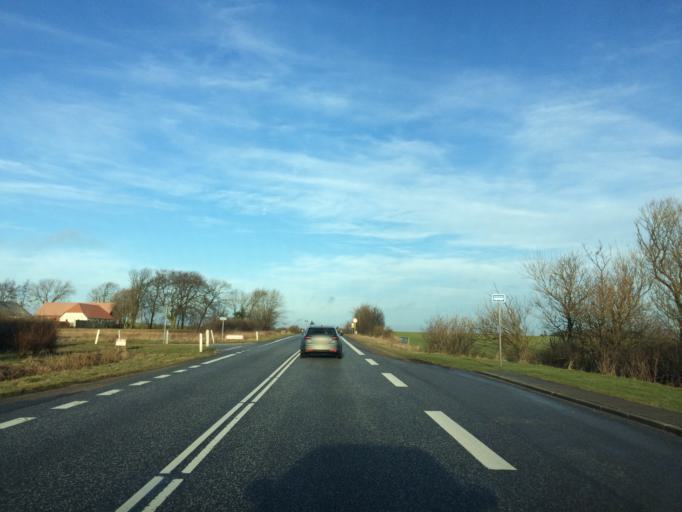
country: DK
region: North Denmark
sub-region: Thisted Kommune
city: Hurup
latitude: 56.7937
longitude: 8.4697
